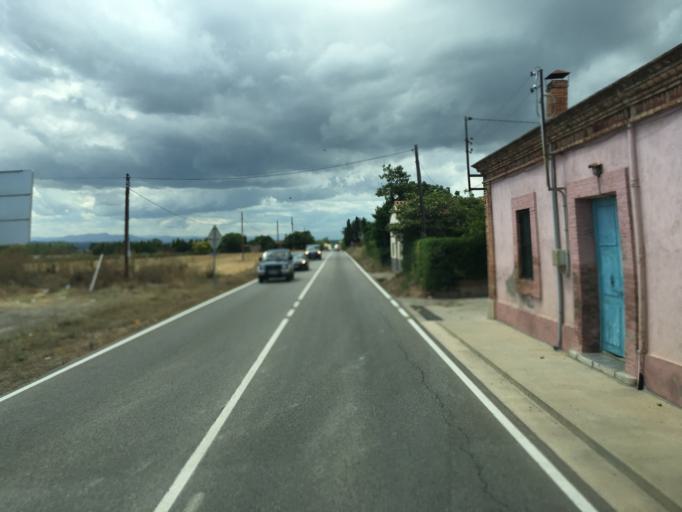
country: ES
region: Catalonia
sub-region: Provincia de Girona
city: Ulla
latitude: 42.0469
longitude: 3.1135
